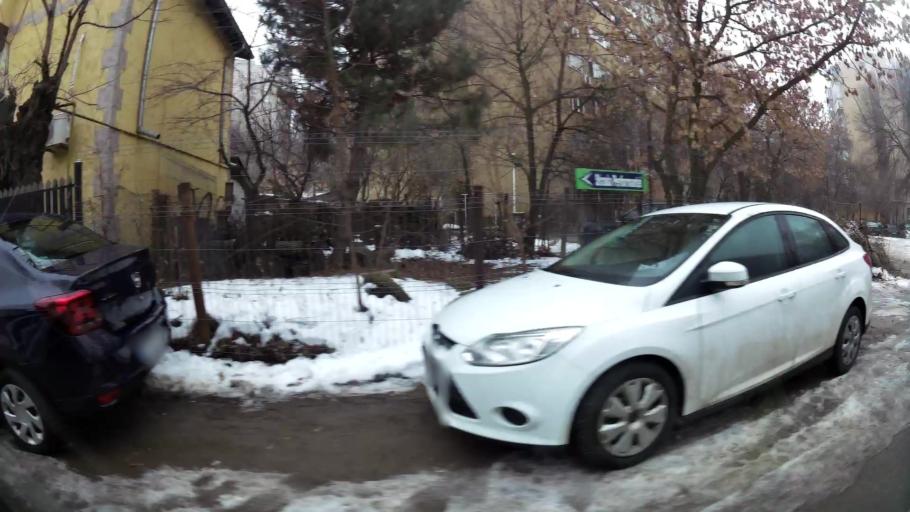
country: RO
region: Ilfov
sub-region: Comuna Chiajna
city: Rosu
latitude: 44.4351
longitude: 26.0174
